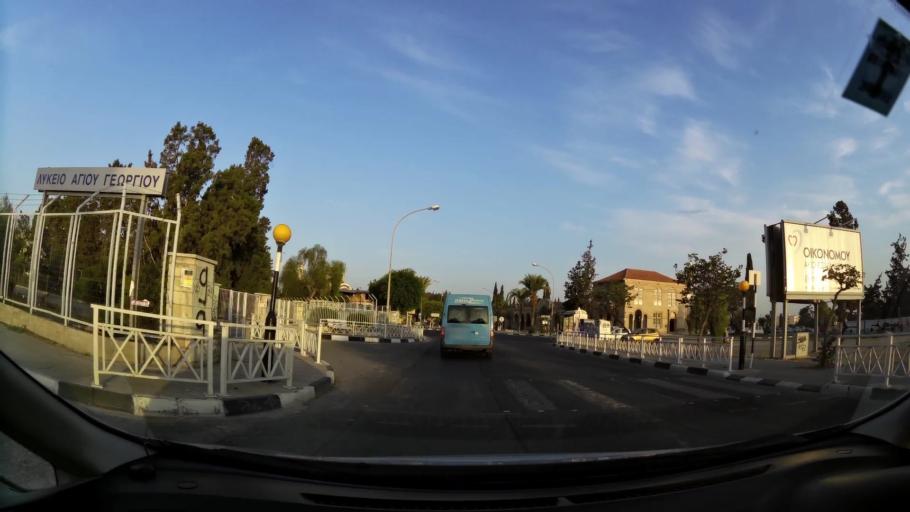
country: CY
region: Larnaka
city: Larnaca
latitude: 34.9230
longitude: 33.6117
